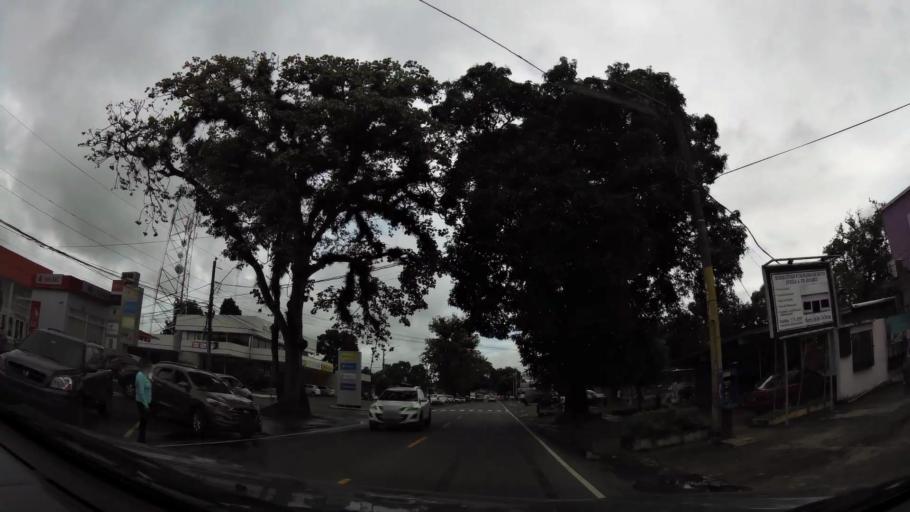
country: PA
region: Chiriqui
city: David
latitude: 8.4408
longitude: -82.4233
